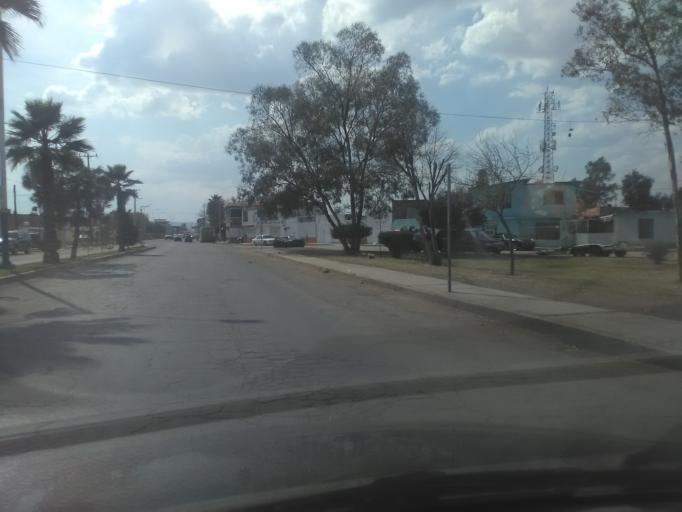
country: MX
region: Durango
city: Victoria de Durango
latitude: 24.0084
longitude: -104.6404
